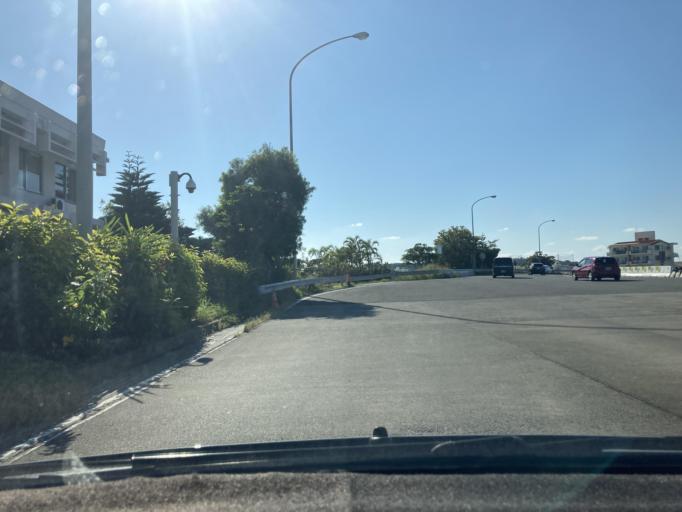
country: JP
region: Okinawa
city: Ginowan
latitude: 26.2483
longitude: 127.7486
